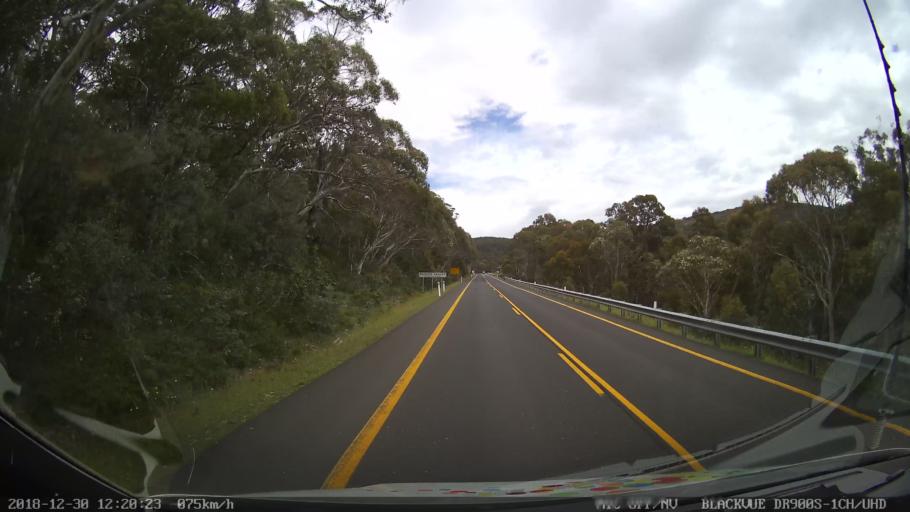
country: AU
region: New South Wales
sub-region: Snowy River
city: Jindabyne
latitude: -36.3471
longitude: 148.5304
